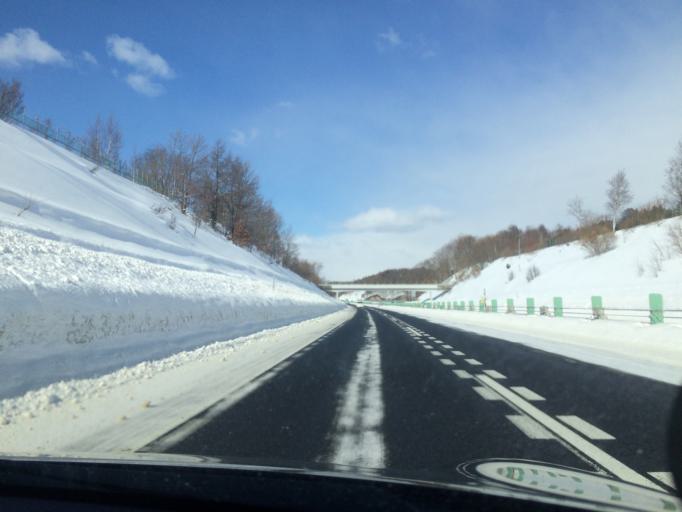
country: JP
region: Hokkaido
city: Kitahiroshima
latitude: 42.9205
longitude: 141.5442
